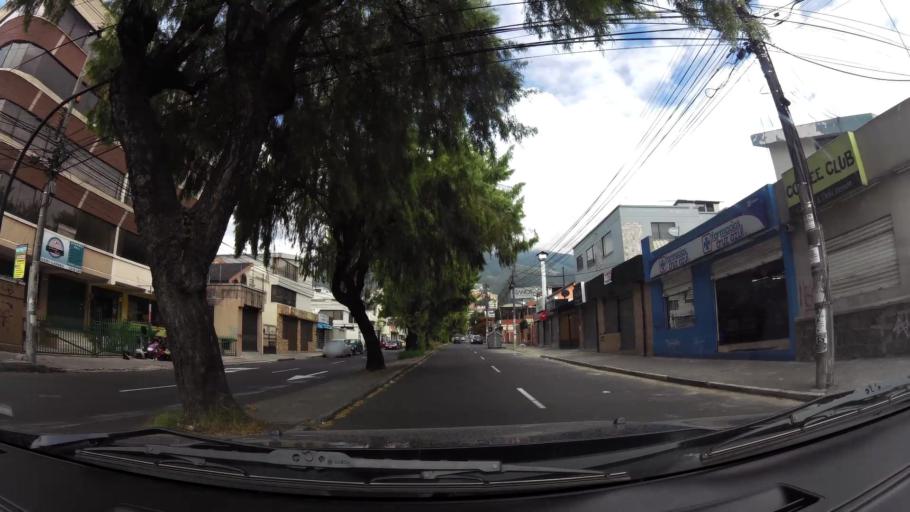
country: EC
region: Pichincha
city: Quito
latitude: -0.1560
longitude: -78.4893
